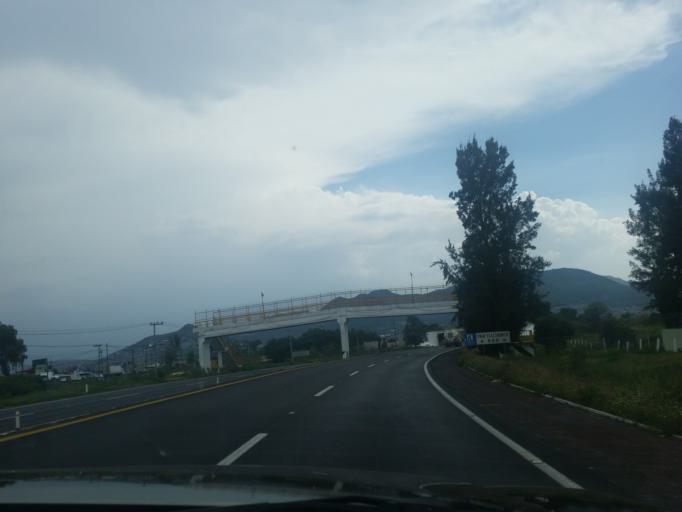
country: MX
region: Mexico
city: Santo Tomas Chiconautla
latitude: 19.6136
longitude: -99.0189
